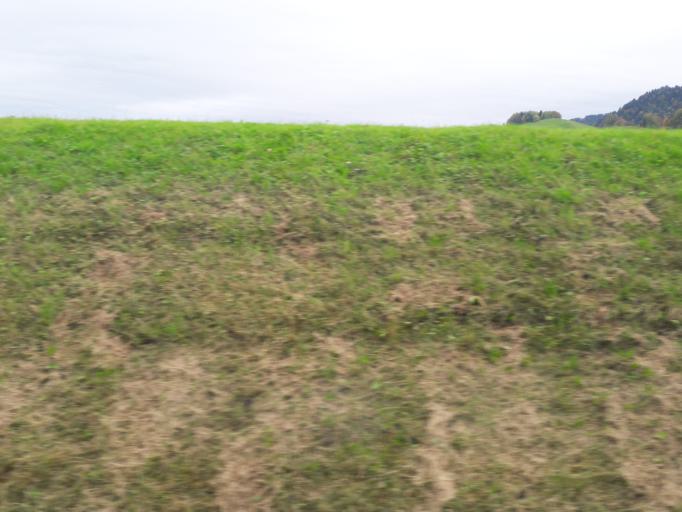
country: CH
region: Zurich
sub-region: Bezirk Horgen
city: Richterswil
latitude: 47.1869
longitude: 8.6887
